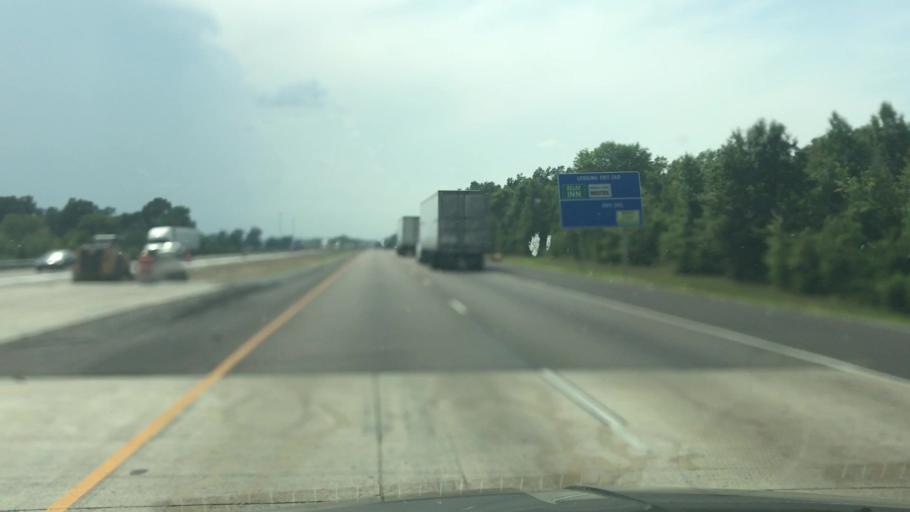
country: US
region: Arkansas
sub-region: Crittenden County
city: Earle
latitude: 35.1338
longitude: -90.4547
